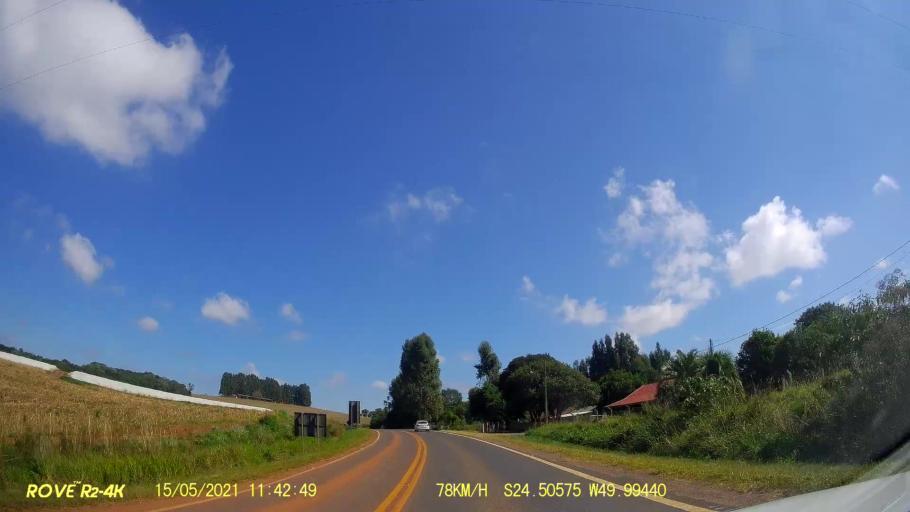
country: BR
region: Parana
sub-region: Pirai Do Sul
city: Pirai do Sul
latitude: -24.5051
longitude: -49.9941
